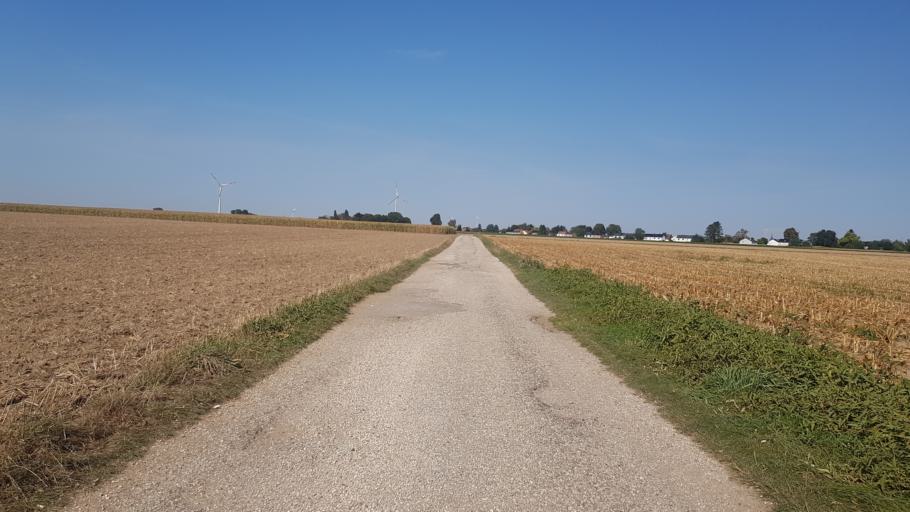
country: DE
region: North Rhine-Westphalia
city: Siersdorf
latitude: 50.8895
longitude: 6.2294
